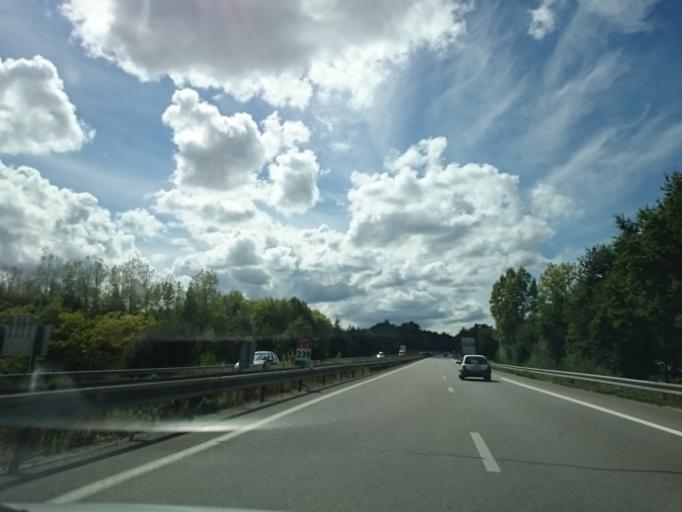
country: FR
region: Pays de la Loire
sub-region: Departement de la Loire-Atlantique
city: Thouare-sur-Loire
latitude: 47.2934
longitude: -1.4557
